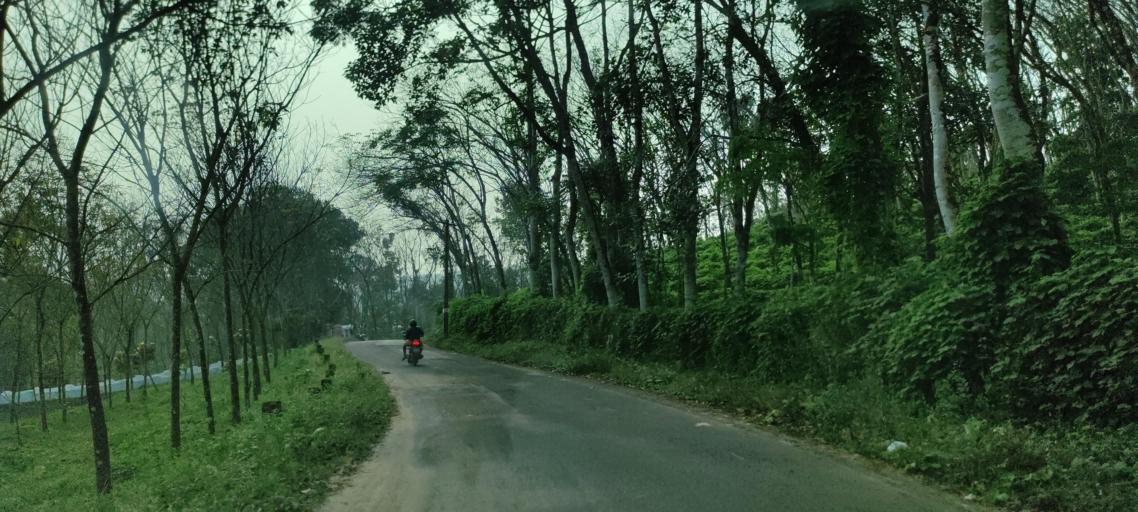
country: IN
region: Kerala
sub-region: Ernakulam
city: Piravam
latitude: 9.8004
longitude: 76.5023
